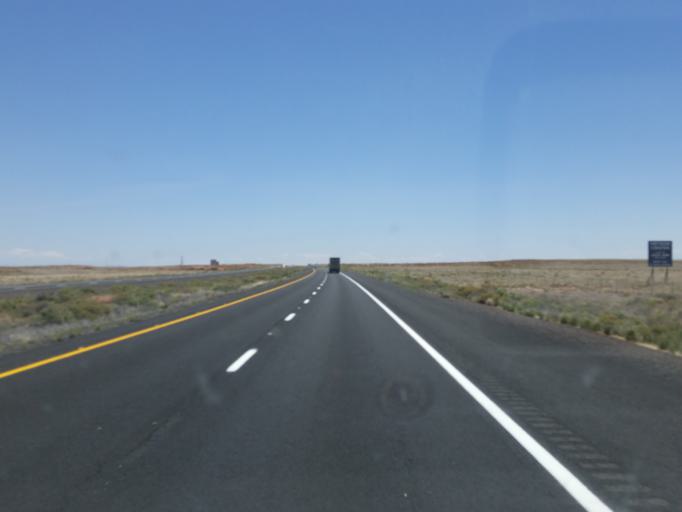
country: US
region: Arizona
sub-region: Coconino County
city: LeChee
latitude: 35.1146
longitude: -111.0729
